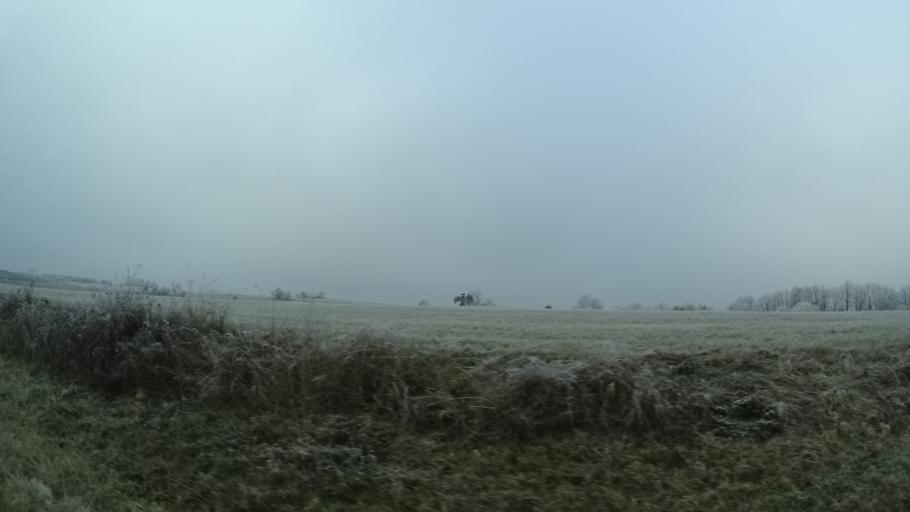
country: DE
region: Bavaria
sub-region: Regierungsbezirk Unterfranken
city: Schollkrippen
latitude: 50.0978
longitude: 9.2615
